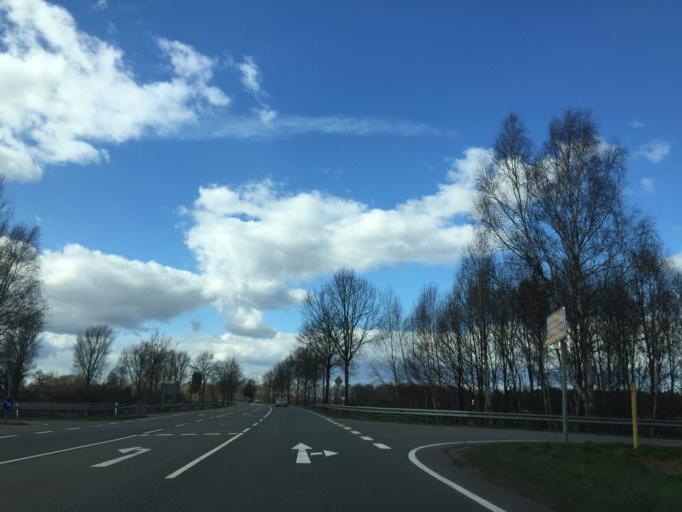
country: DE
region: Lower Saxony
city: Broeckel
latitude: 52.5351
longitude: 10.2141
